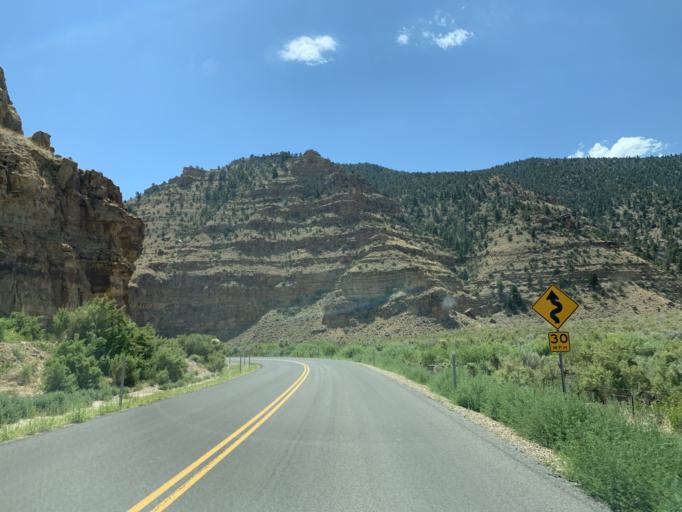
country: US
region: Utah
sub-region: Carbon County
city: East Carbon City
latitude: 39.8083
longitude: -110.2706
